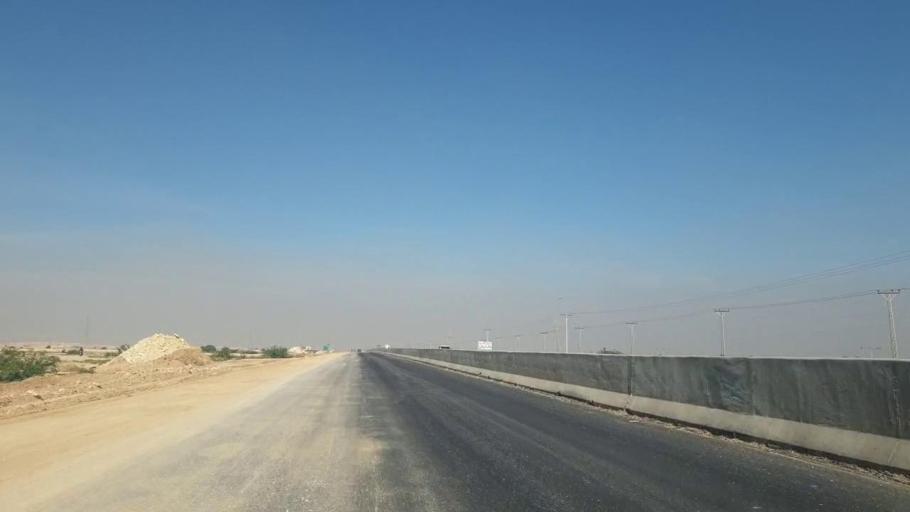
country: PK
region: Sindh
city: Jamshoro
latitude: 25.5145
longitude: 68.2738
